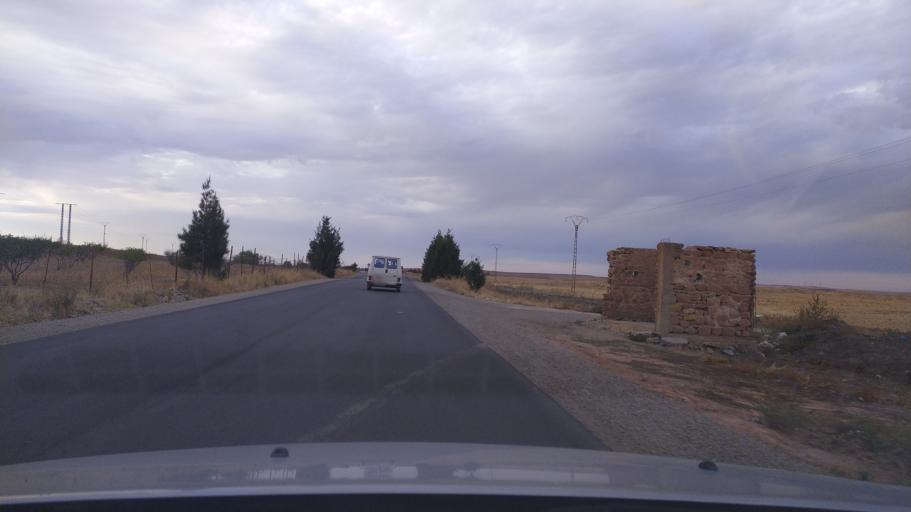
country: DZ
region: Tiaret
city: Frenda
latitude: 35.0127
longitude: 1.1154
